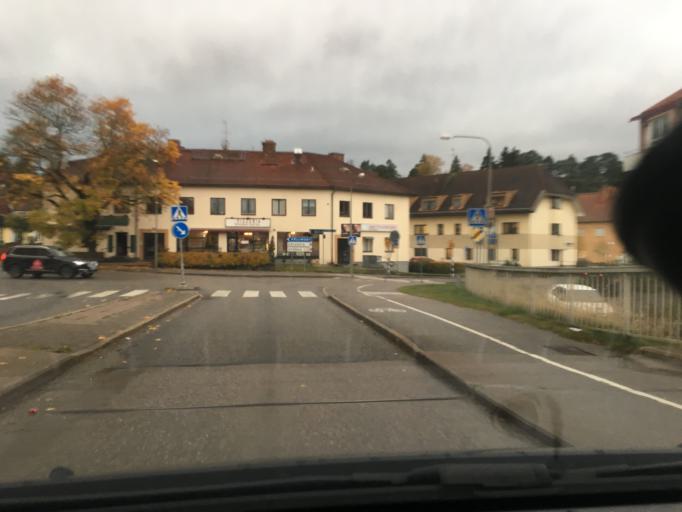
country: SE
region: Stockholm
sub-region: Stockholms Kommun
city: Kista
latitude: 59.3813
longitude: 17.9003
